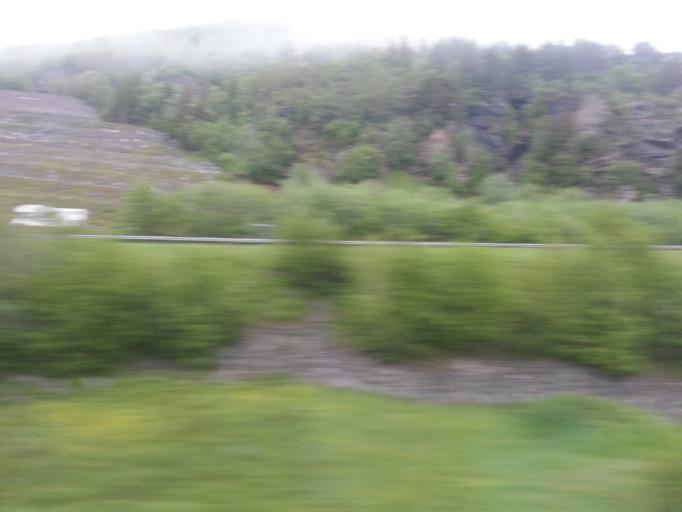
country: NO
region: Sor-Trondelag
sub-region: Oppdal
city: Oppdal
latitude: 62.4458
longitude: 9.5858
